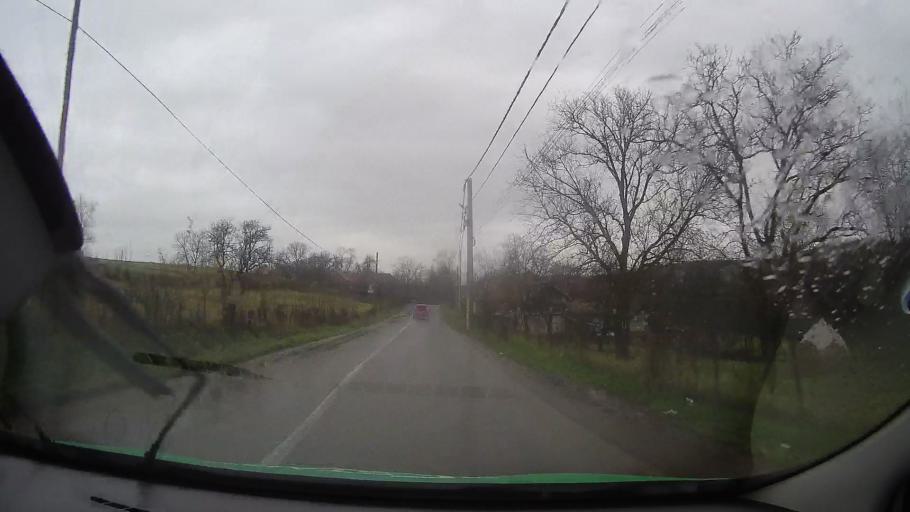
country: RO
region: Mures
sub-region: Comuna Vatava
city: Vatava
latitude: 46.9316
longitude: 24.7681
